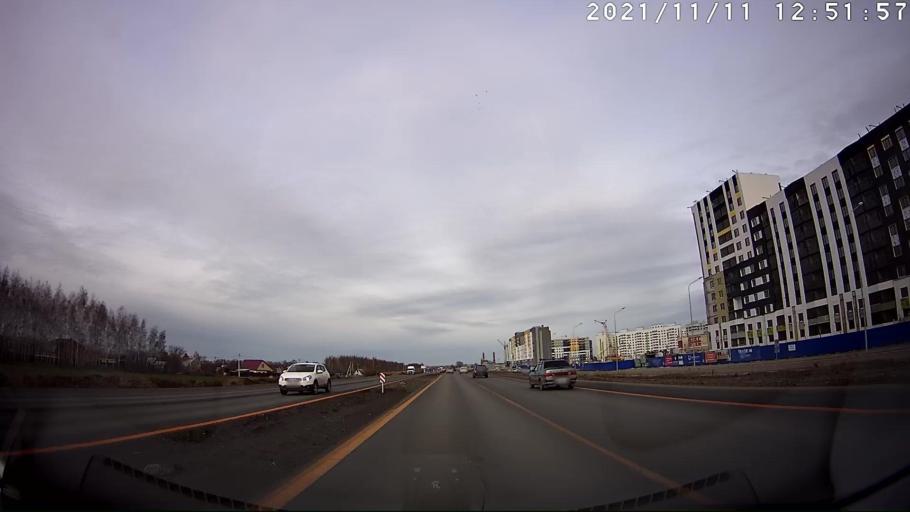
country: RU
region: Ulyanovsk
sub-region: Ulyanovskiy Rayon
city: Ulyanovsk
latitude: 54.2777
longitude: 48.2600
